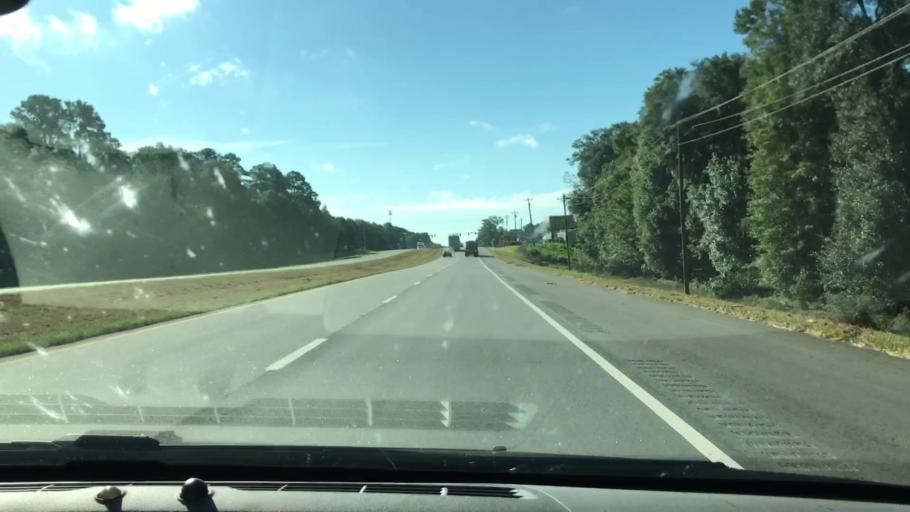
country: US
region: Georgia
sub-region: Lee County
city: Leesburg
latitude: 31.6663
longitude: -84.2831
